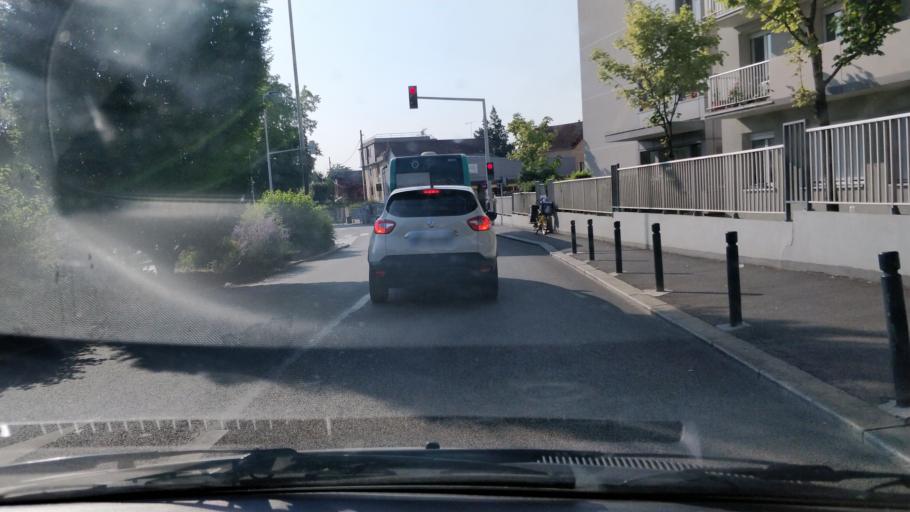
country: FR
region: Ile-de-France
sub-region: Departement de Seine-Saint-Denis
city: Villemomble
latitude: 48.8835
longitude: 2.5115
